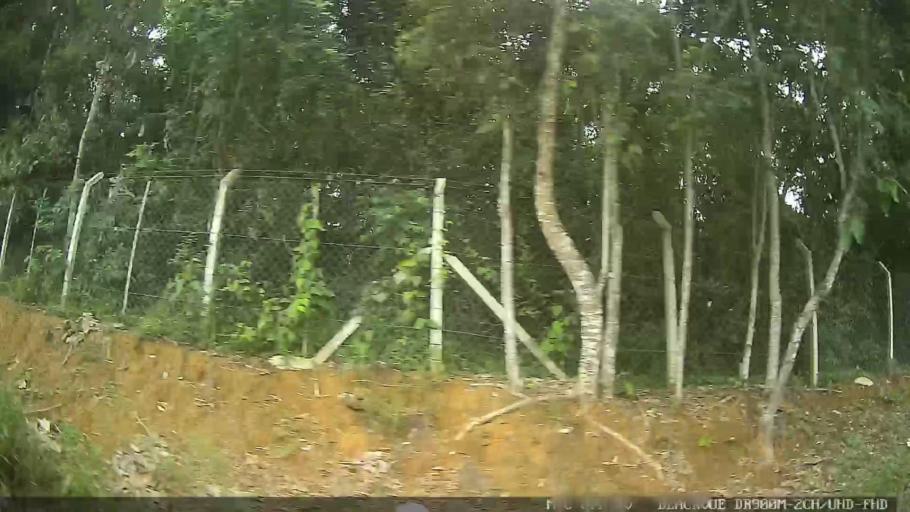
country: BR
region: Sao Paulo
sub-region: Suzano
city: Suzano
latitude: -23.6281
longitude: -46.2837
